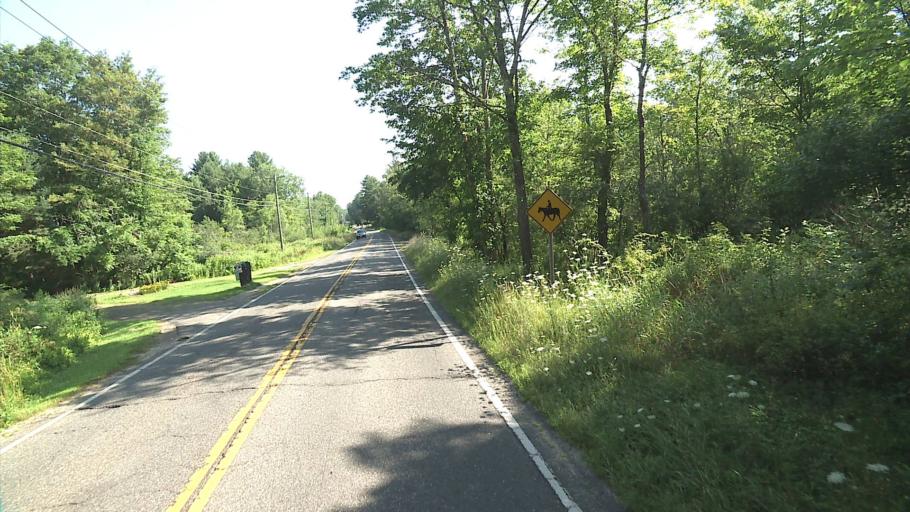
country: US
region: Connecticut
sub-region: Litchfield County
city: Winsted
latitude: 41.8707
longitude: -73.0682
